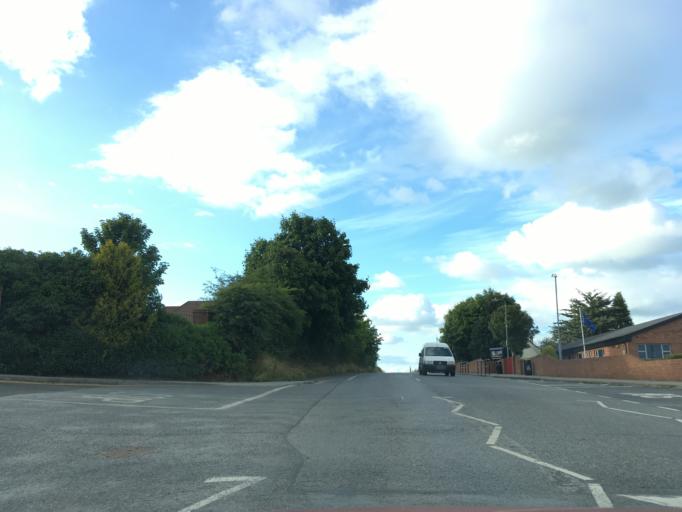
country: IE
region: Munster
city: Cashel
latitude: 52.5097
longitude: -7.8858
